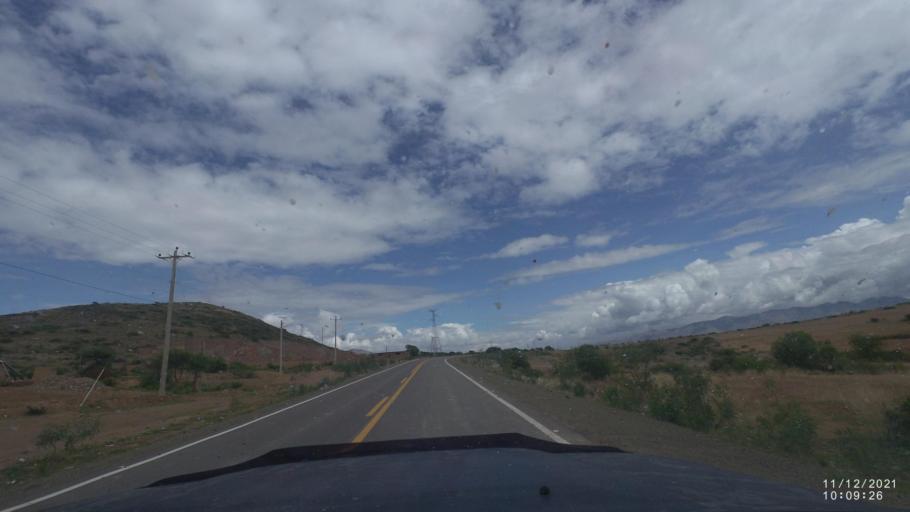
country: BO
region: Cochabamba
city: Tarata
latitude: -17.6567
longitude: -65.9702
